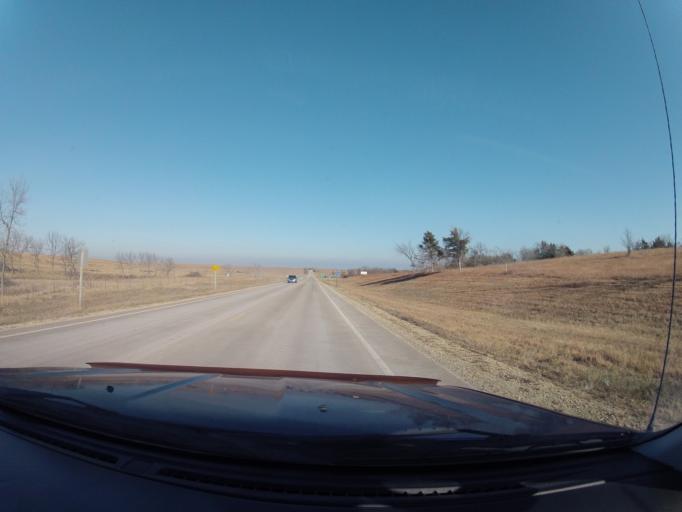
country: US
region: Kansas
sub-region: Marshall County
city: Blue Rapids
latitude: 39.4329
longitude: -96.7643
